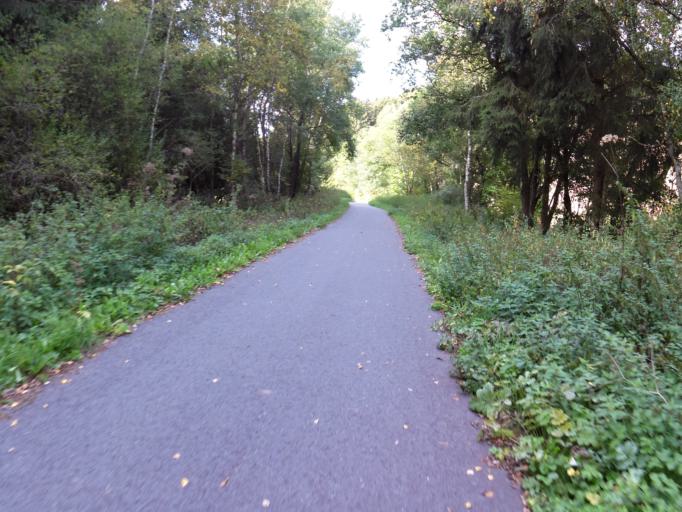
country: BE
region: Wallonia
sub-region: Province de Liege
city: Saint-Vith
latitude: 50.2390
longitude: 6.1566
